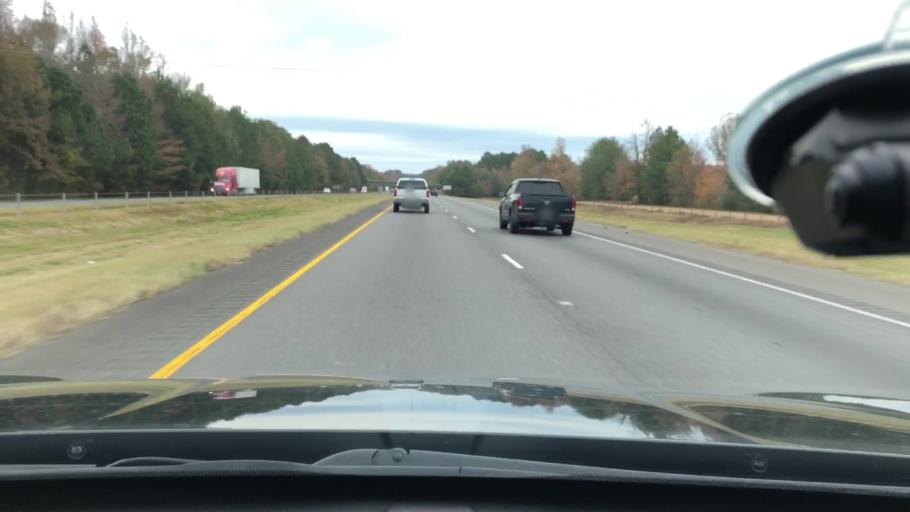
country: US
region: Arkansas
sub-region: Clark County
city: Gurdon
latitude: 34.0181
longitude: -93.1619
